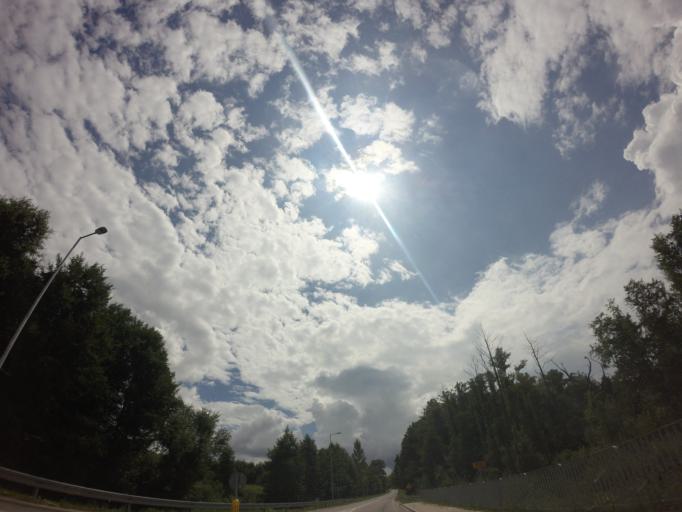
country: PL
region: Masovian Voivodeship
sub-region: Powiat lipski
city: Solec Nad Wisla
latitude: 51.1258
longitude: 21.7608
